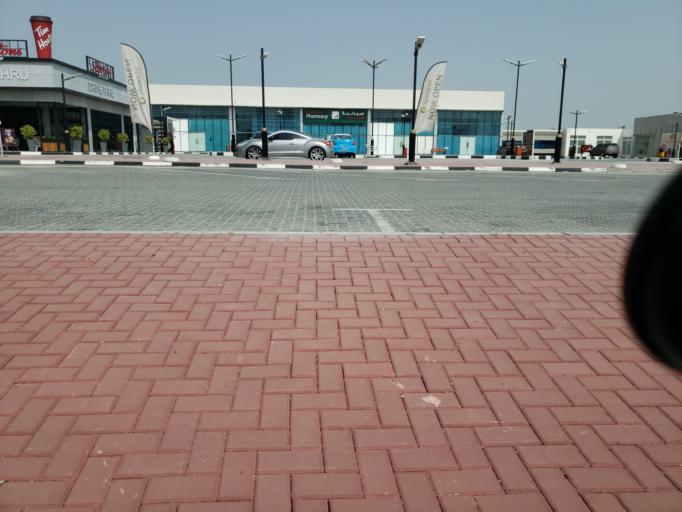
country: AE
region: Ajman
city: Ajman
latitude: 25.4177
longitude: 55.4879
